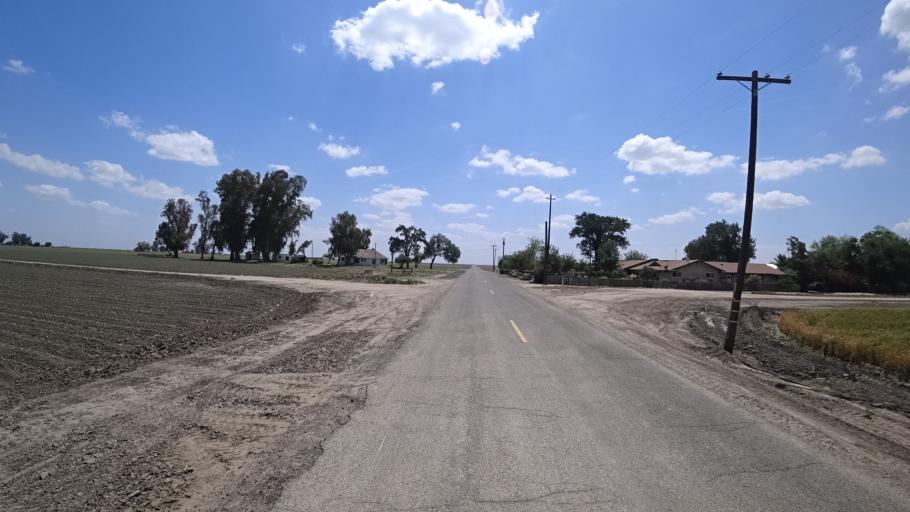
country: US
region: California
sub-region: Kings County
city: Stratford
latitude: 36.1639
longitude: -119.8249
